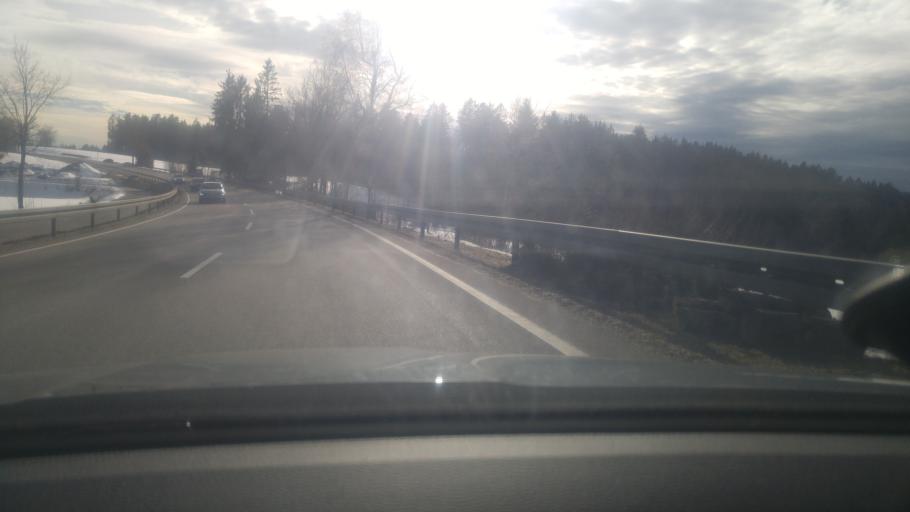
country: DE
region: Baden-Wuerttemberg
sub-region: Freiburg Region
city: Hochenschwand
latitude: 47.7104
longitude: 8.1450
